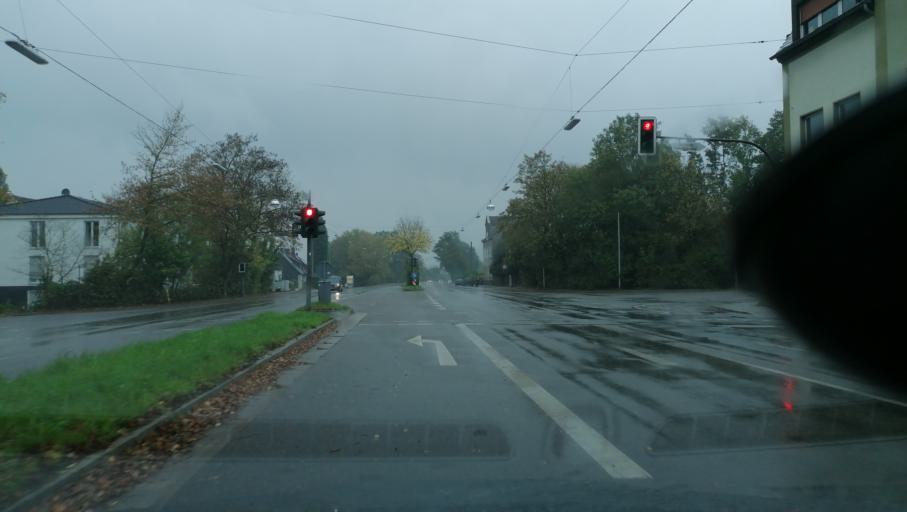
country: DE
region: North Rhine-Westphalia
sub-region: Regierungsbezirk Munster
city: Recklinghausen
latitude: 51.5870
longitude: 7.1818
